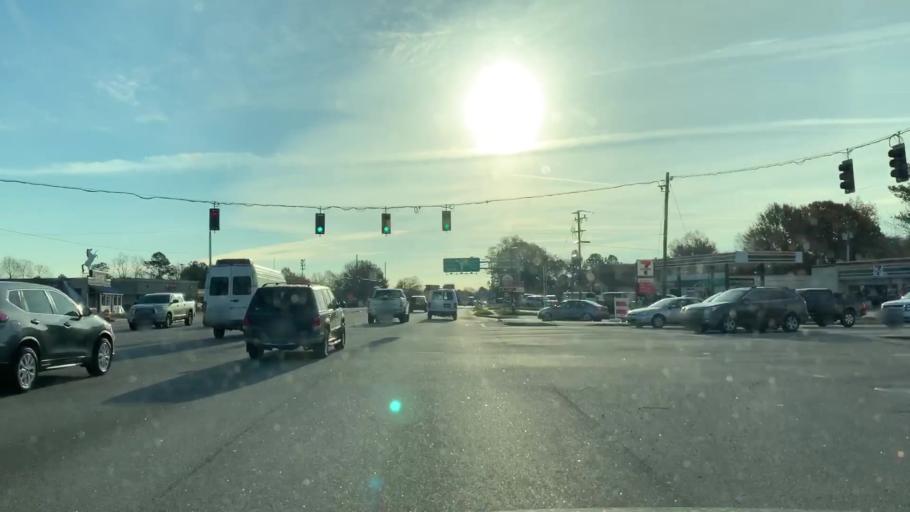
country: US
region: Virginia
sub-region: City of Chesapeake
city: Chesapeake
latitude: 36.7974
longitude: -76.1751
